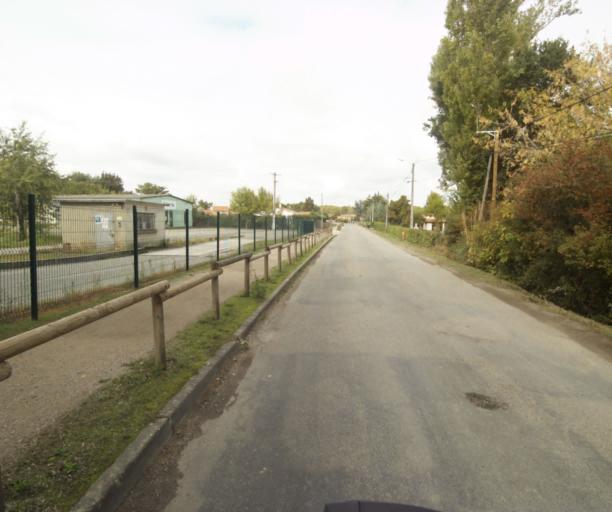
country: FR
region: Midi-Pyrenees
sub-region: Departement du Tarn-et-Garonne
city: Montech
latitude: 43.9567
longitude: 1.2446
